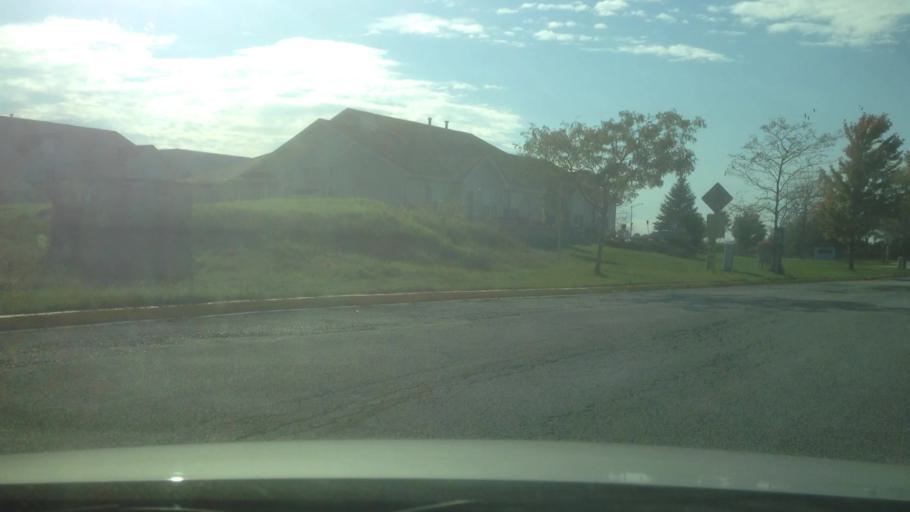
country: US
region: Illinois
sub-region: Will County
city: Monee
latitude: 41.4238
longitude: -87.7565
